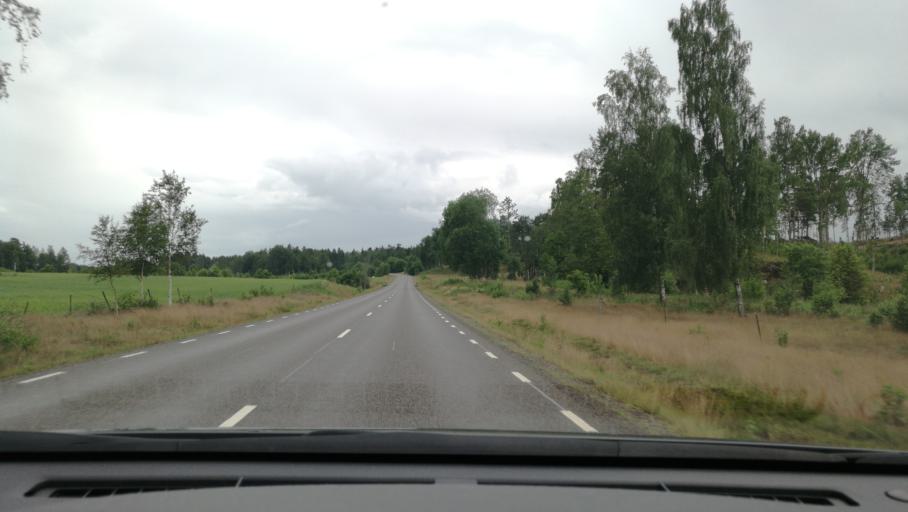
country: SE
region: OEstergoetland
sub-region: Norrkopings Kommun
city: Svartinge
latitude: 58.7794
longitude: 15.9667
